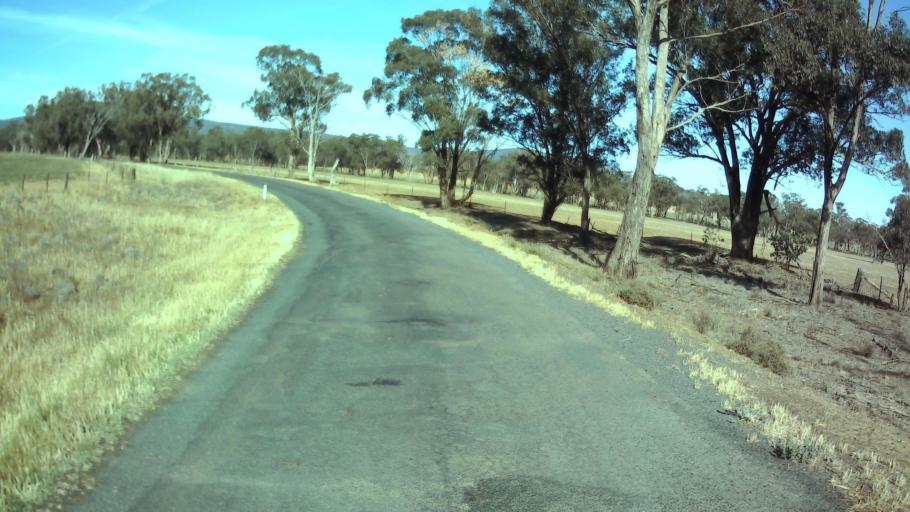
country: AU
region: New South Wales
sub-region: Weddin
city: Grenfell
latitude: -33.9049
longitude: 148.0854
